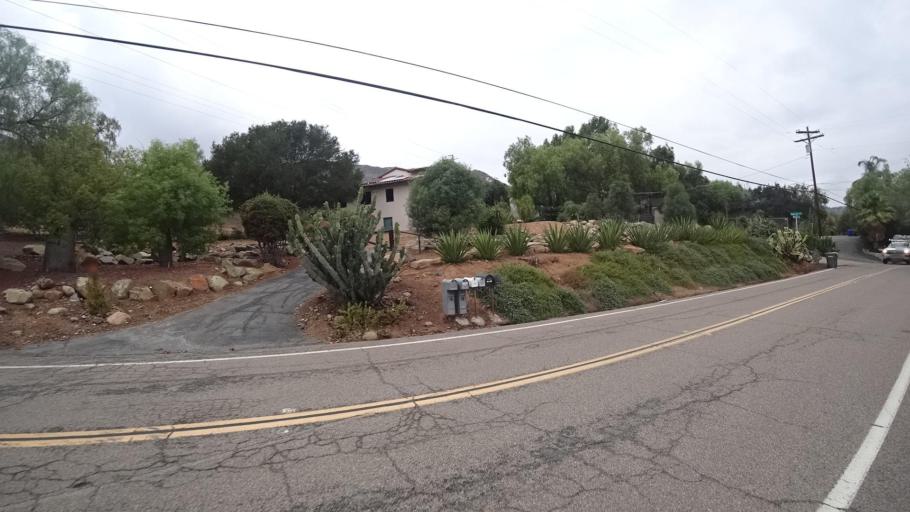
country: US
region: California
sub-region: San Diego County
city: Escondido
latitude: 33.0618
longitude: -117.1224
